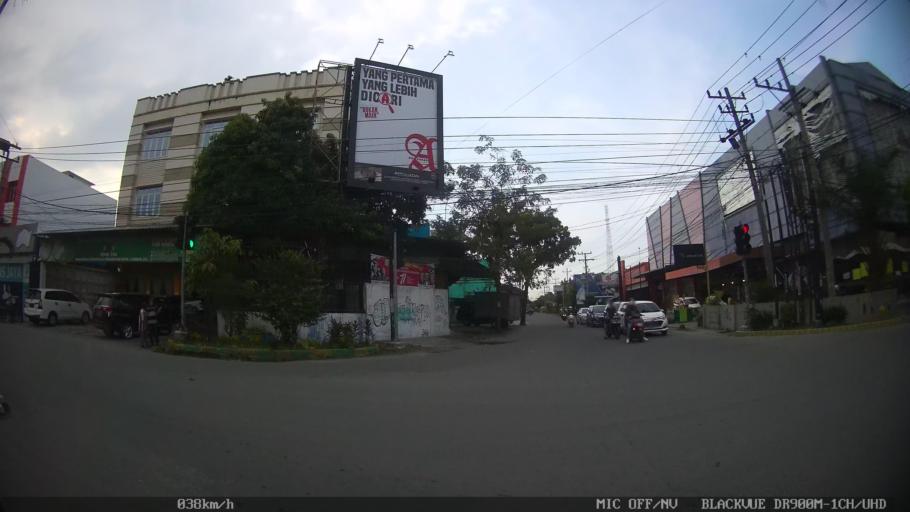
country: ID
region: North Sumatra
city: Medan
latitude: 3.6078
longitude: 98.6765
